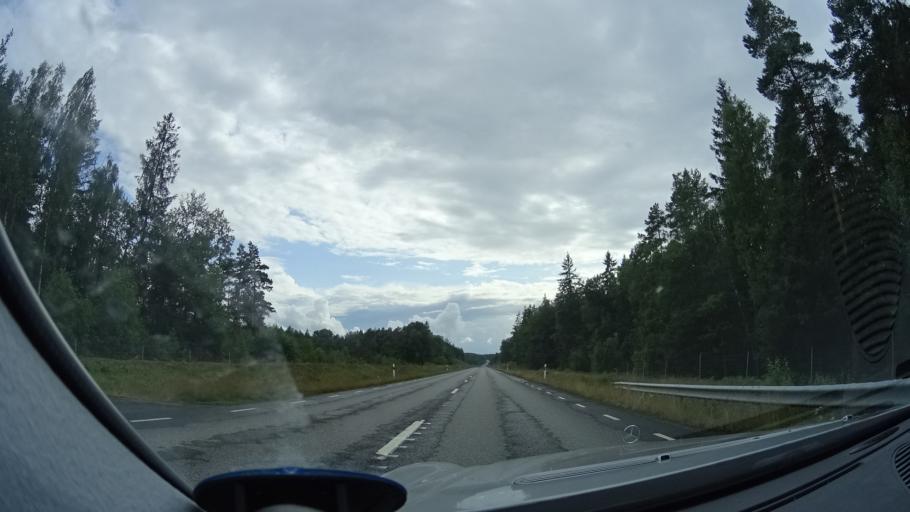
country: SE
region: Blekinge
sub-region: Karlshamns Kommun
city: Svangsta
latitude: 56.2696
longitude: 14.8533
